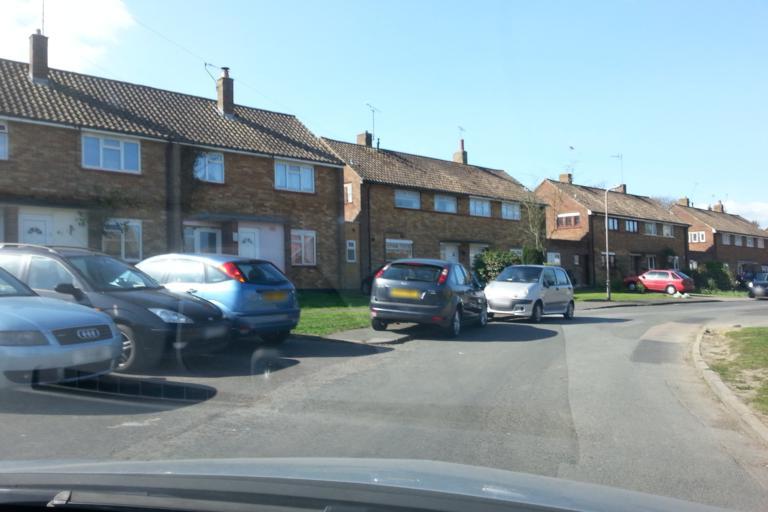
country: GB
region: England
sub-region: Essex
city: Hadleigh
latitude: 51.5612
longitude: 0.5965
